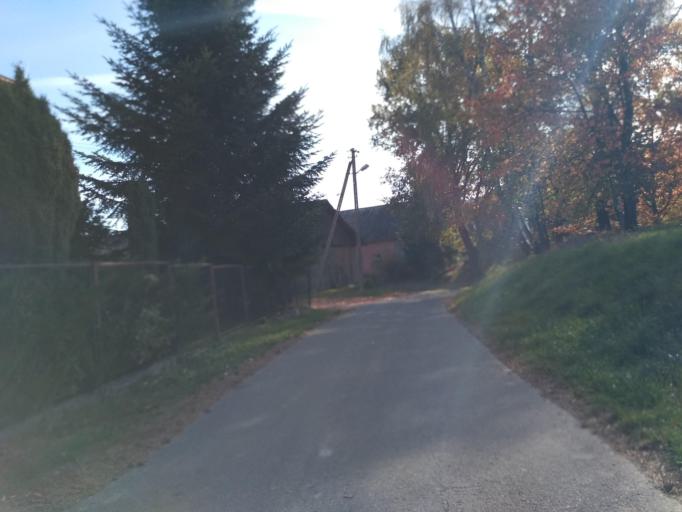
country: PL
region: Subcarpathian Voivodeship
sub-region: Powiat ropczycko-sedziszowski
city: Iwierzyce
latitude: 50.0507
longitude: 21.7580
